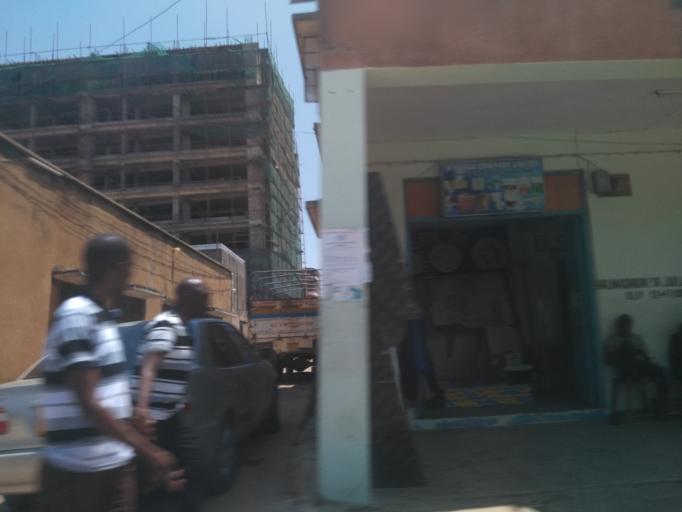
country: TZ
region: Dodoma
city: Dodoma
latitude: -6.1797
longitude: 35.7481
